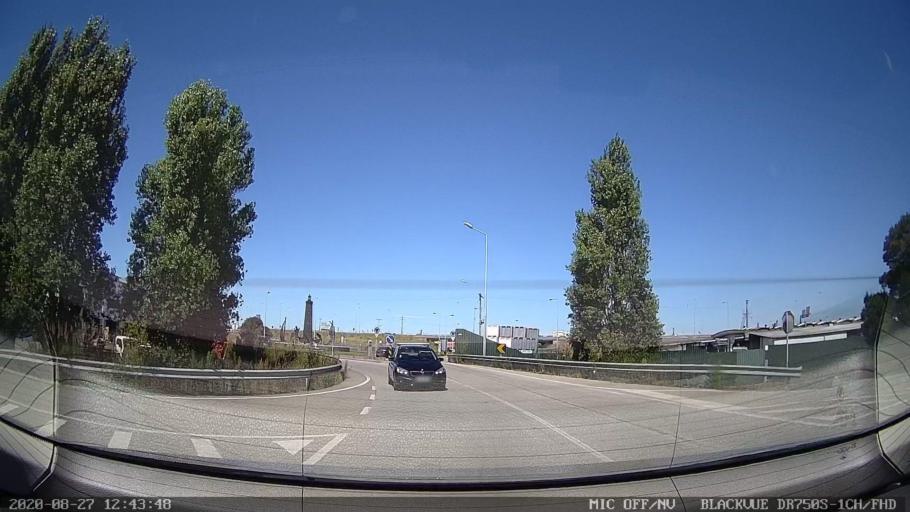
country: PT
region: Aveiro
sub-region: Ilhavo
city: Gafanha da Nazare
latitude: 40.6301
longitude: -8.6879
